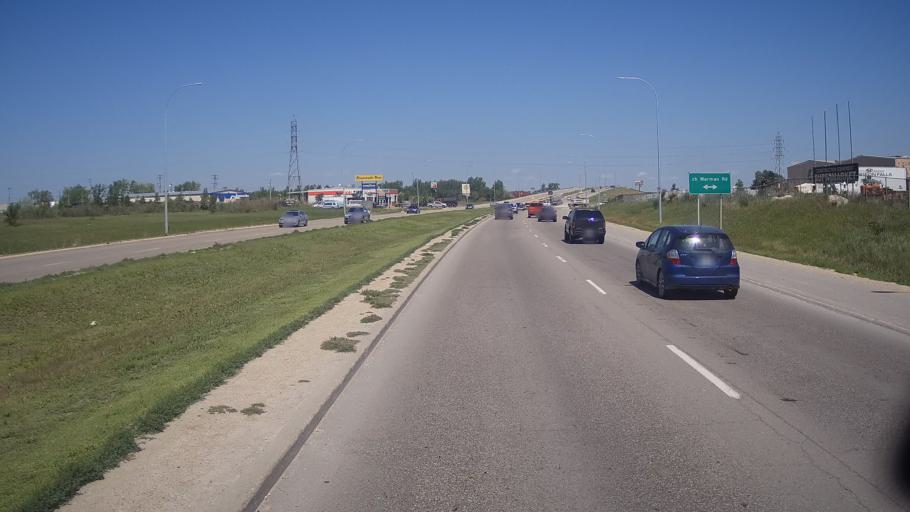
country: CA
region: Manitoba
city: Winnipeg
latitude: 49.8887
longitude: -97.0722
